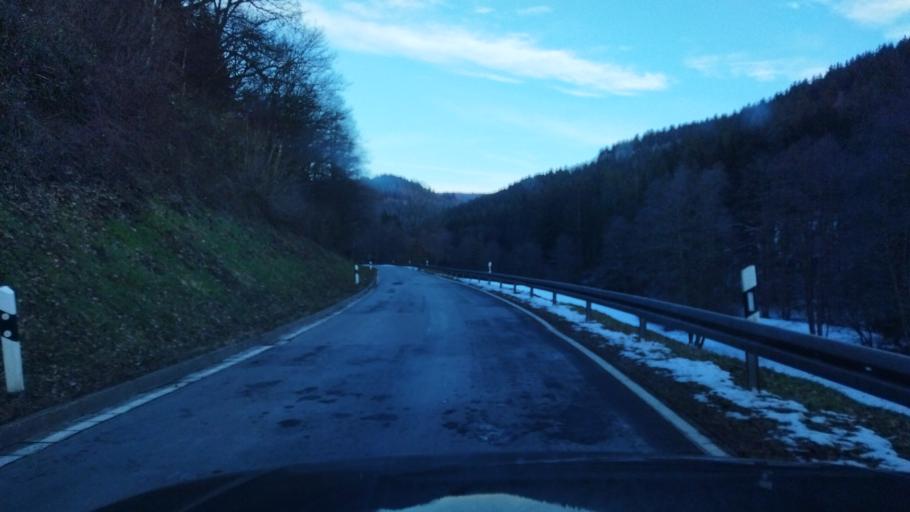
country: DE
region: Baden-Wuerttemberg
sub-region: Karlsruhe Region
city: Eberbach
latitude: 49.4989
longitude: 9.0272
